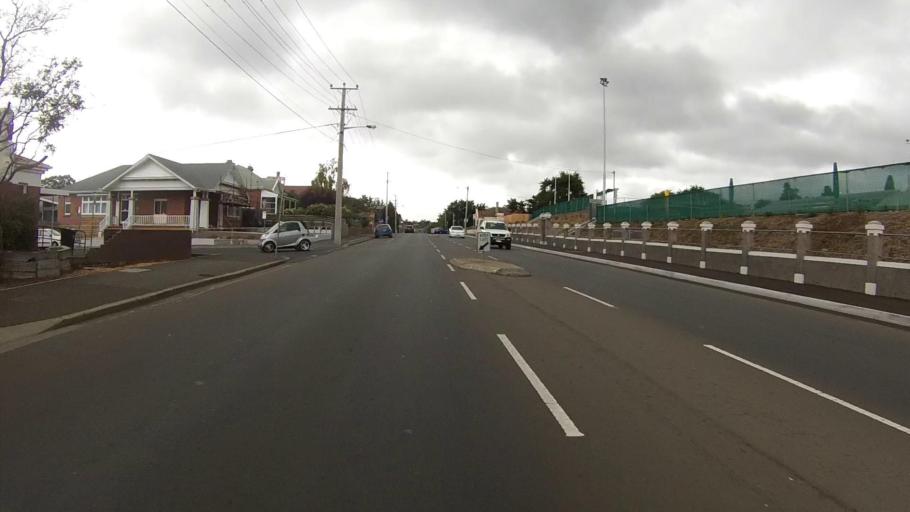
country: AU
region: Tasmania
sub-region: Glenorchy
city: Moonah
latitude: -42.8522
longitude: 147.2993
